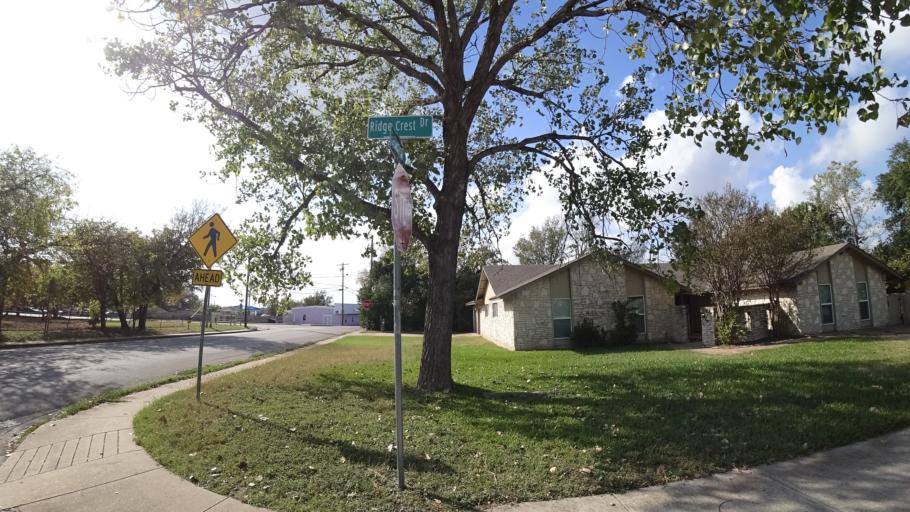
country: US
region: Texas
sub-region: Williamson County
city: Round Rock
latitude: 30.5024
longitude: -97.6746
